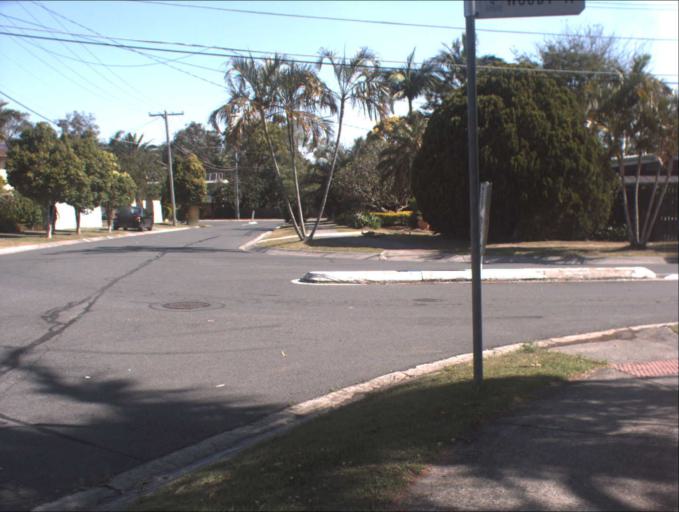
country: AU
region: Queensland
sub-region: Logan
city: Logan City
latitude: -27.6579
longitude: 153.1102
